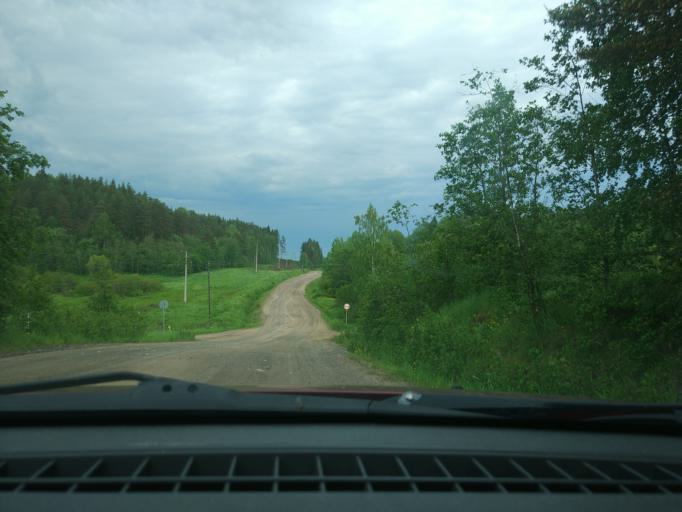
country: RU
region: Leningrad
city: Kuznechnoye
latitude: 61.2708
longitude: 29.8355
